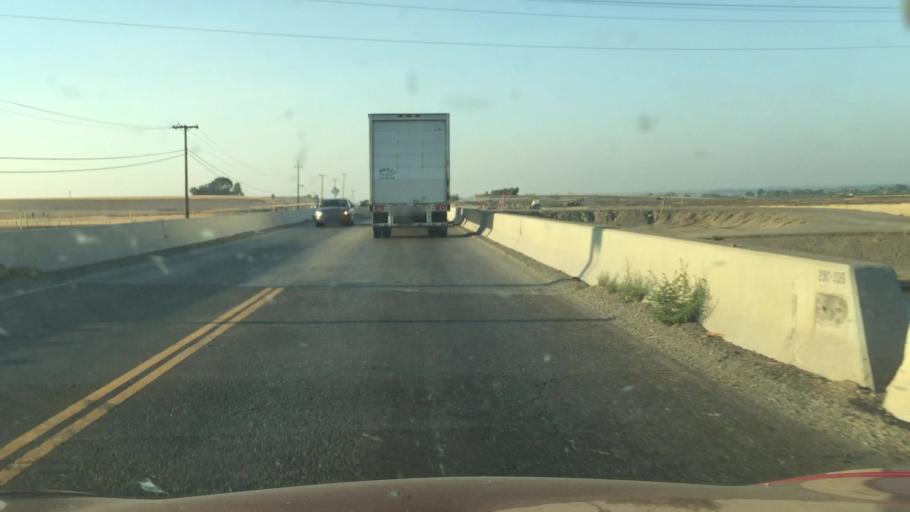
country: US
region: California
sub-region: San Joaquin County
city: Mountain House
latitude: 37.7300
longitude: -121.5313
